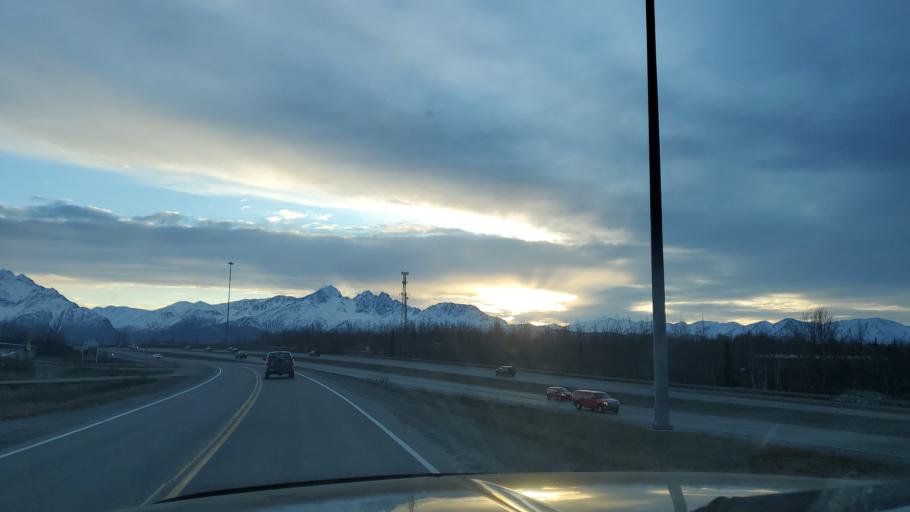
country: US
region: Alaska
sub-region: Matanuska-Susitna Borough
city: Lakes
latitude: 61.5661
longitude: -149.3072
